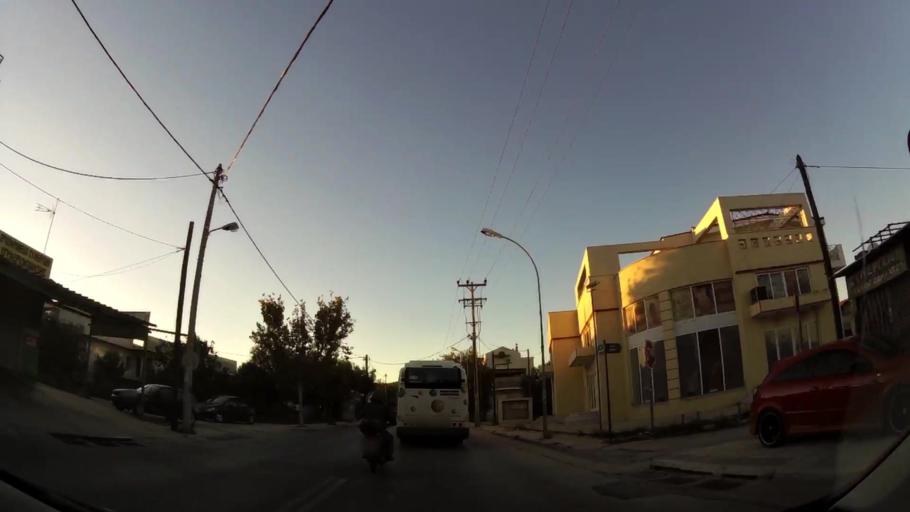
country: GR
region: Attica
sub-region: Nomarchia Dytikis Attikis
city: Ano Liosia
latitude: 38.0762
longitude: 23.7038
